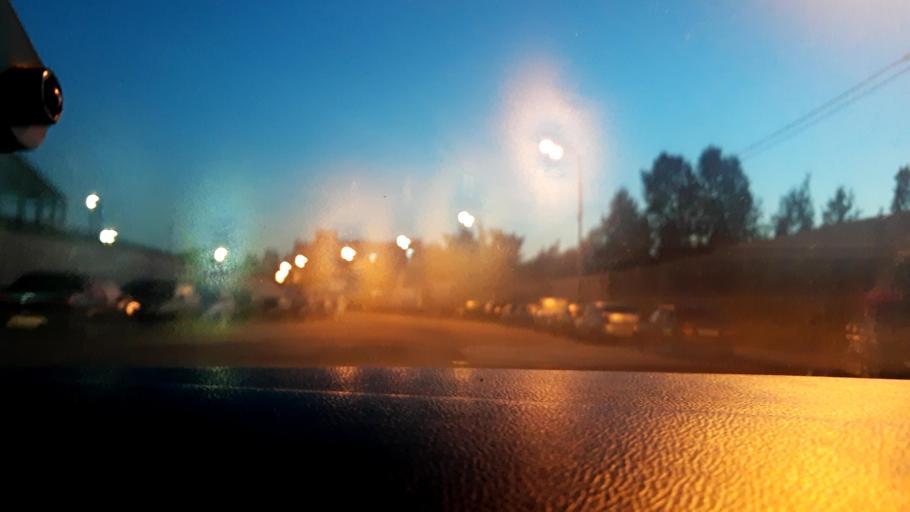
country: RU
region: Moscow
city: Otradnoye
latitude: 55.8499
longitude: 37.6067
